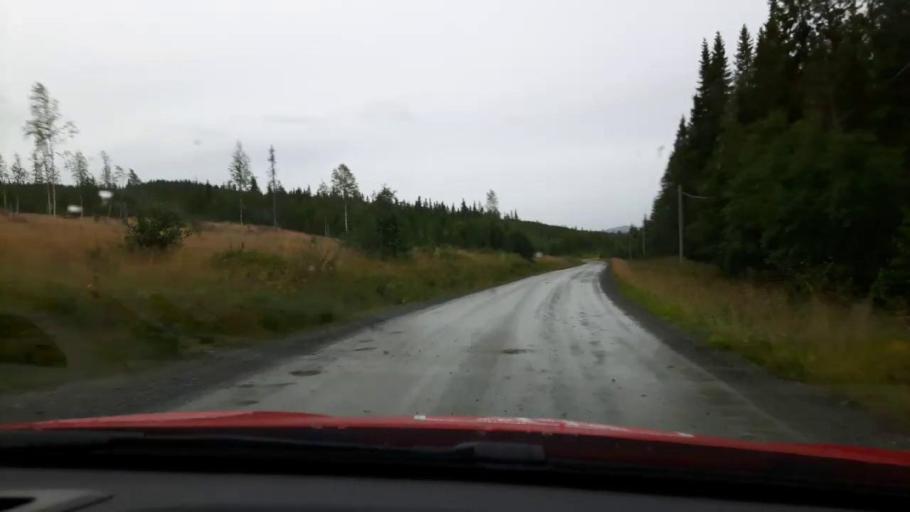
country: SE
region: Jaemtland
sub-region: Are Kommun
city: Are
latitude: 63.4248
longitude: 12.8175
